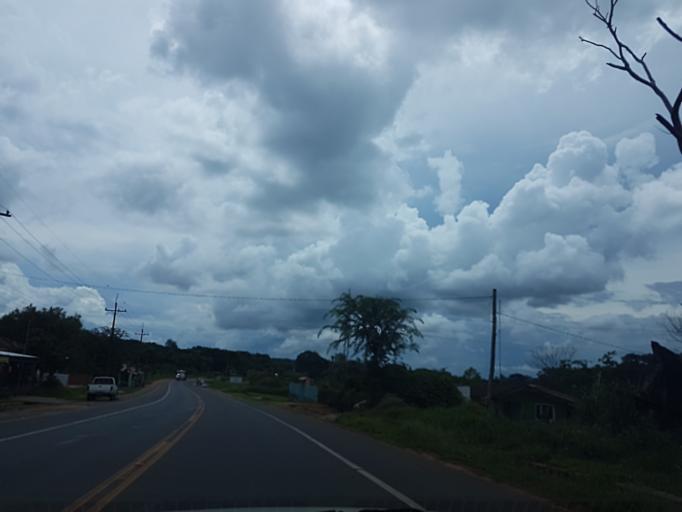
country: PY
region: Central
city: Limpio
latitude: -25.2370
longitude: -57.4377
